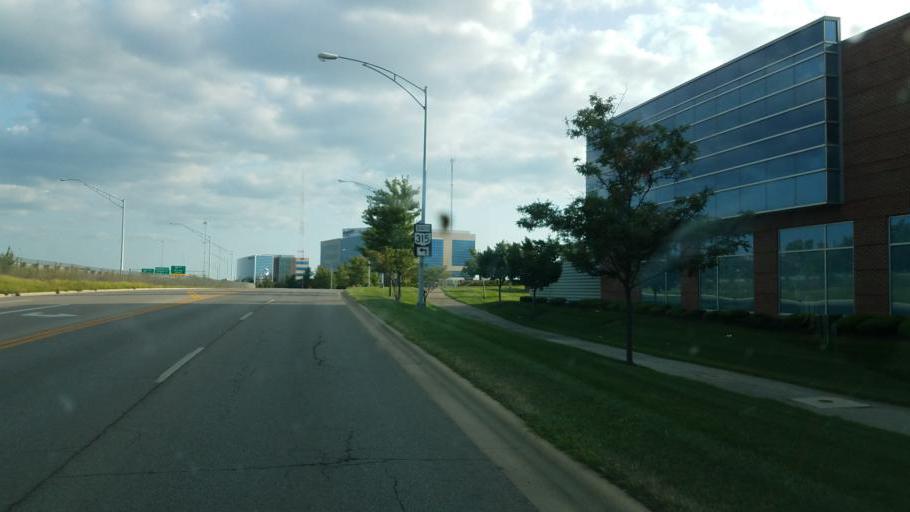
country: US
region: Ohio
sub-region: Franklin County
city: Grandview Heights
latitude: 39.9833
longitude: -83.0228
